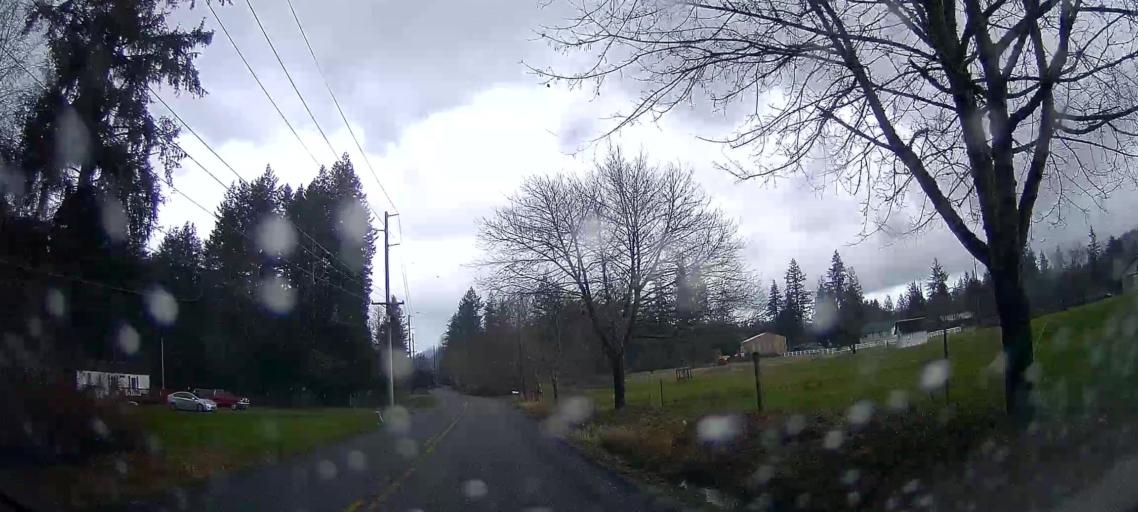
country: US
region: Washington
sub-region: Whatcom County
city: Sudden Valley
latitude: 48.6072
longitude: -122.3338
